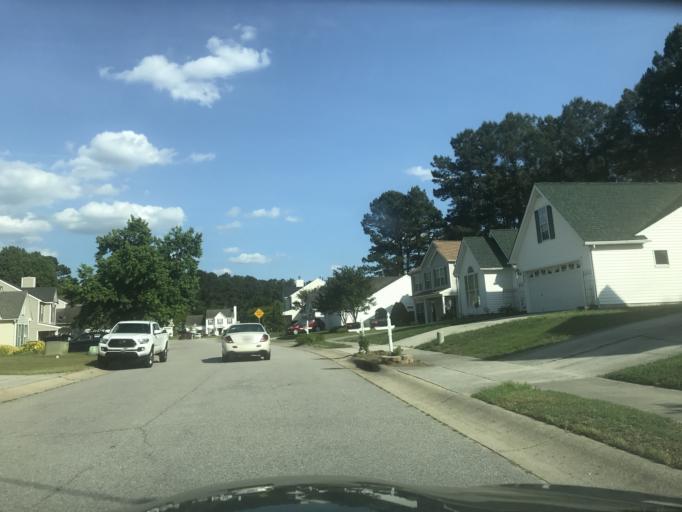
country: US
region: North Carolina
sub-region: Wake County
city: Knightdale
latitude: 35.8502
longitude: -78.5527
